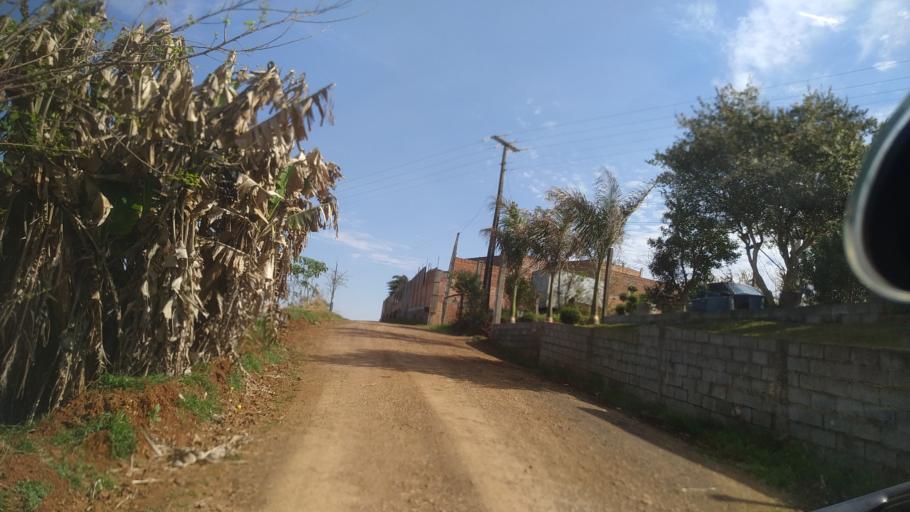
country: BR
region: Santa Catarina
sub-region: Chapeco
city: Chapeco
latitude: -27.1194
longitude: -52.5893
